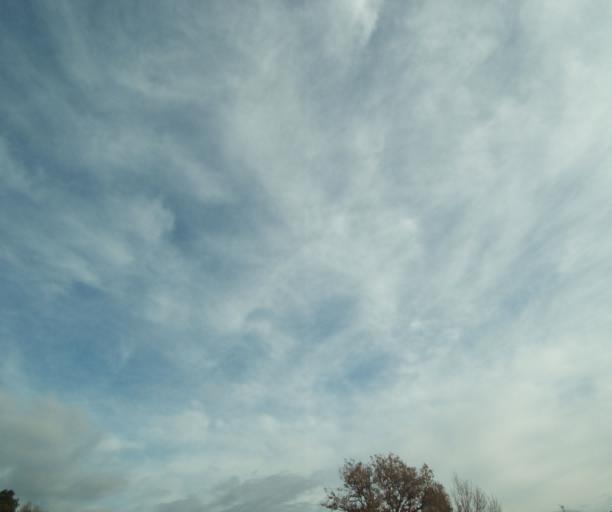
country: FR
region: Provence-Alpes-Cote d'Azur
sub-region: Departement du Var
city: Cabasse
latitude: 43.4034
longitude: 6.2392
